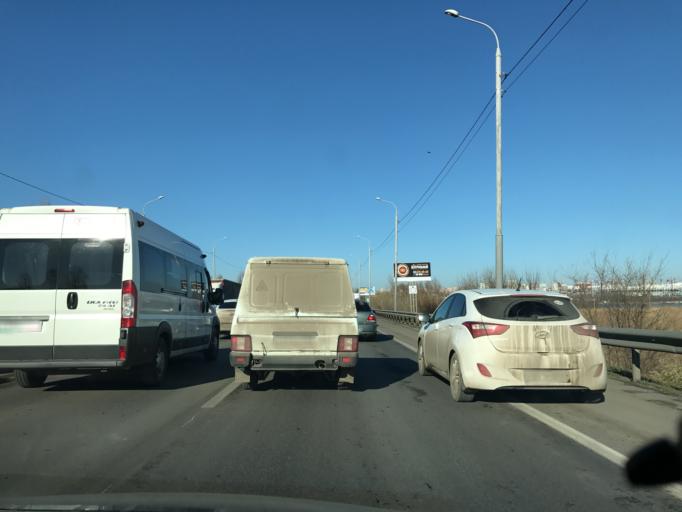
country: RU
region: Rostov
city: Rostov-na-Donu
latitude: 47.1914
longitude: 39.7341
